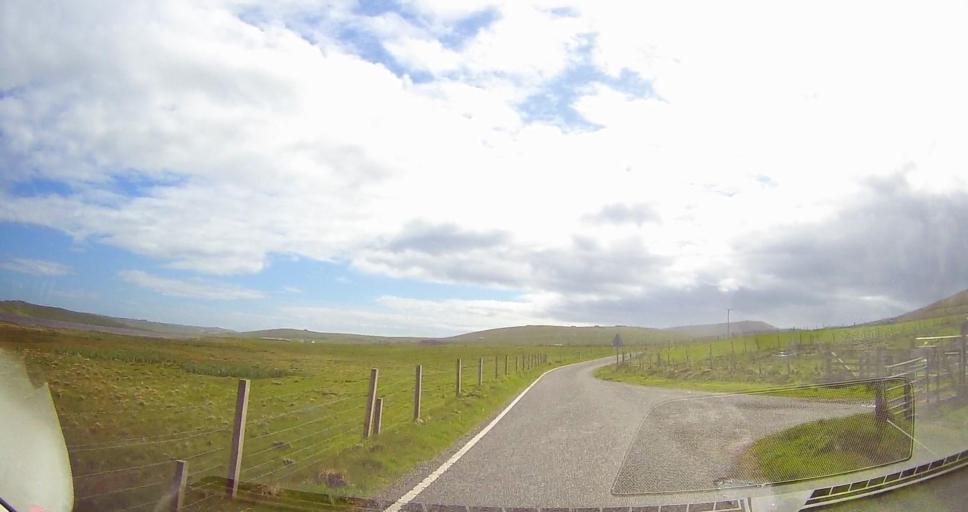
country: GB
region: Scotland
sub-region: Shetland Islands
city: Sandwick
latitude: 59.9418
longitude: -1.3451
